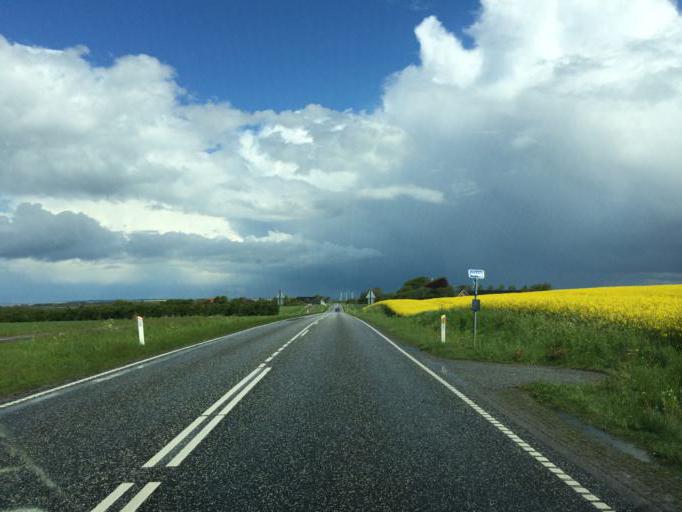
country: DK
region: Central Jutland
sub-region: Holstebro Kommune
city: Vinderup
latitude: 56.4537
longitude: 8.7653
